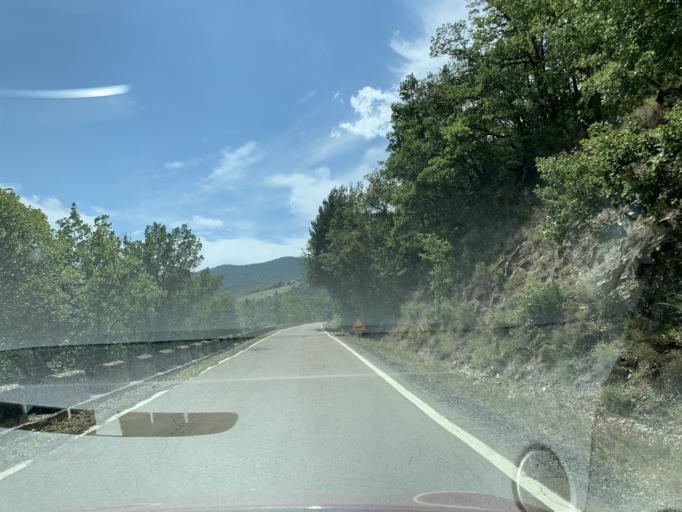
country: ES
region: Aragon
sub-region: Provincia de Huesca
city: Jasa
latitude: 42.6253
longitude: -0.6544
